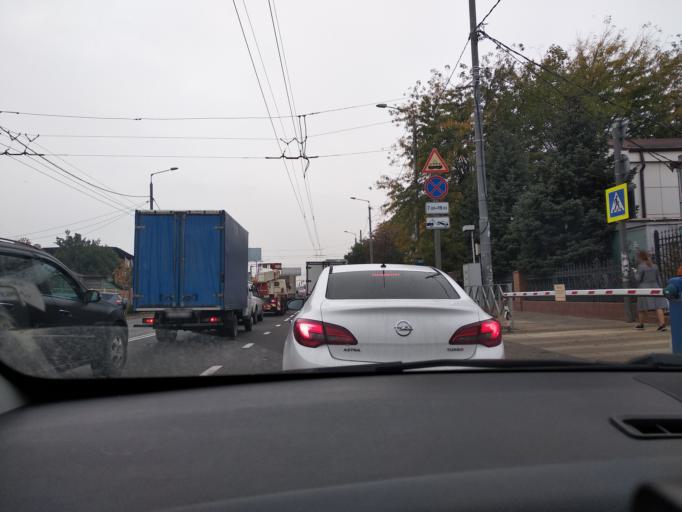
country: RU
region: Krasnodarskiy
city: Krasnodar
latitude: 45.0413
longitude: 38.9559
